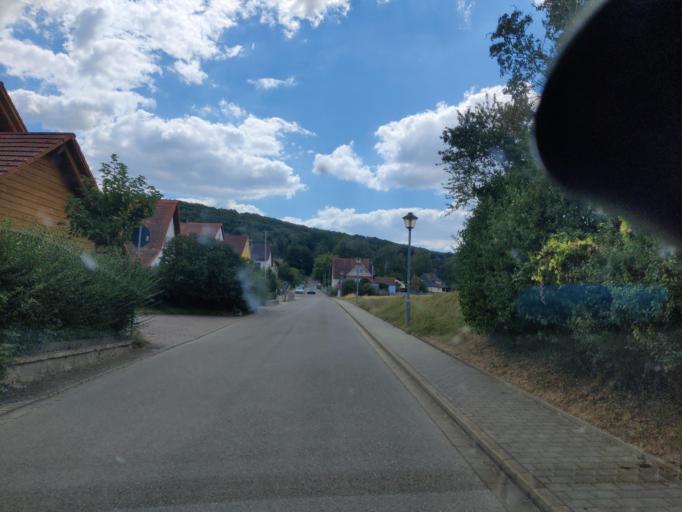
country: DE
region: Bavaria
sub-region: Regierungsbezirk Mittelfranken
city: Thalmassing
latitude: 49.0834
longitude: 11.2131
